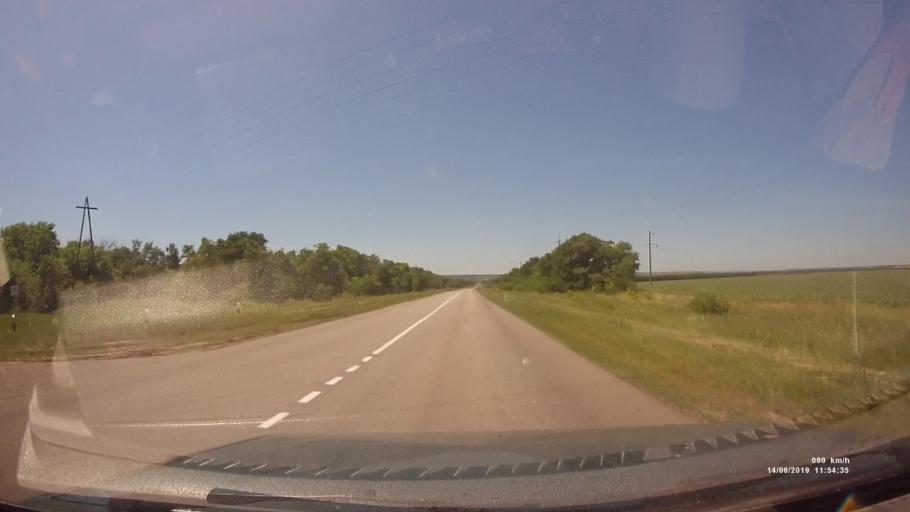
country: RU
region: Rostov
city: Kazanskaya
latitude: 49.8178
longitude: 41.1919
